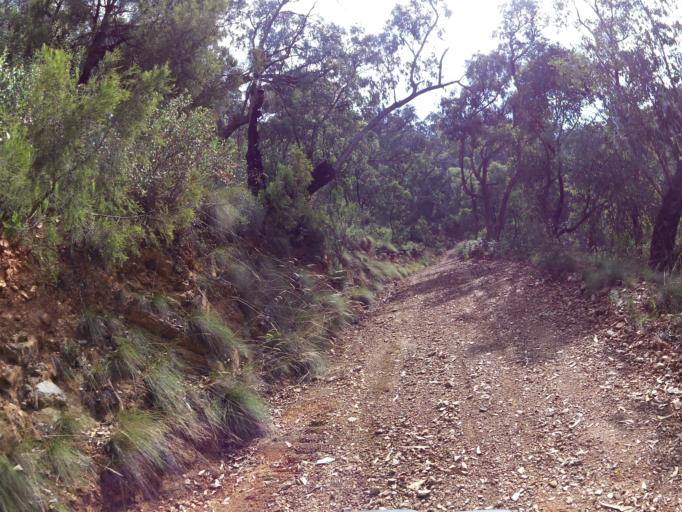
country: AU
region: Victoria
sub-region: Alpine
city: Mount Beauty
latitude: -36.7784
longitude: 147.0128
